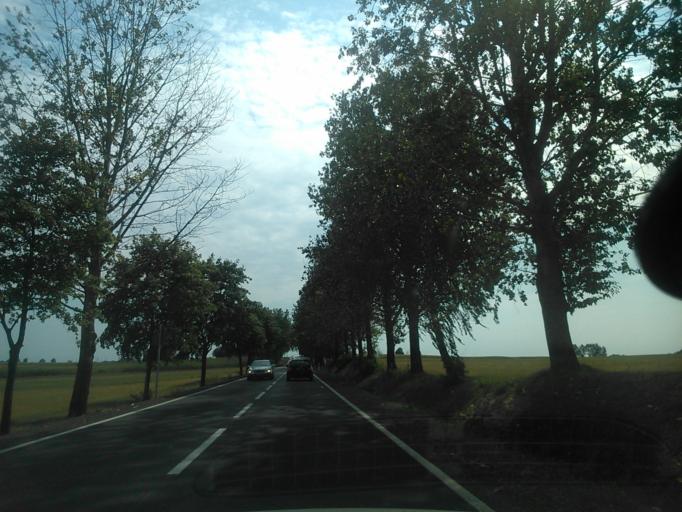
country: PL
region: Warmian-Masurian Voivodeship
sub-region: Powiat dzialdowski
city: Lidzbark
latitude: 53.2431
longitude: 19.9251
